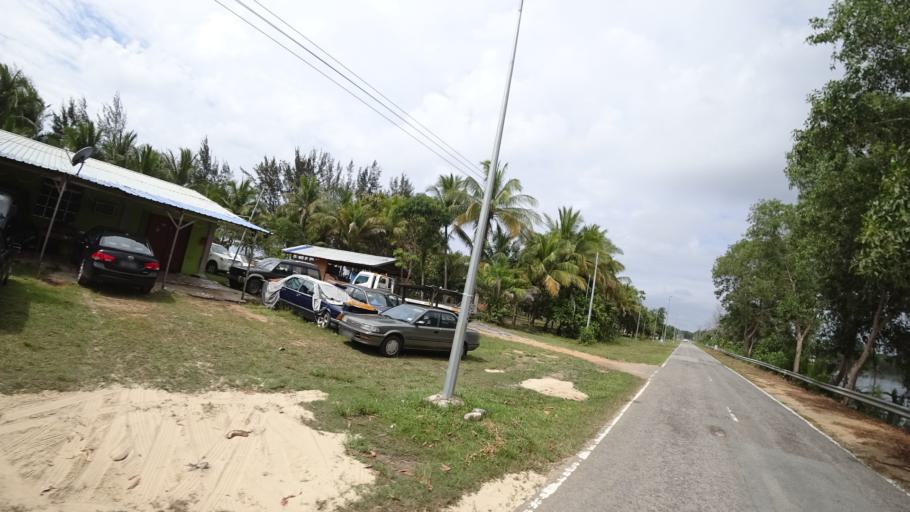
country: BN
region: Tutong
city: Tutong
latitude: 4.7894
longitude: 114.6169
